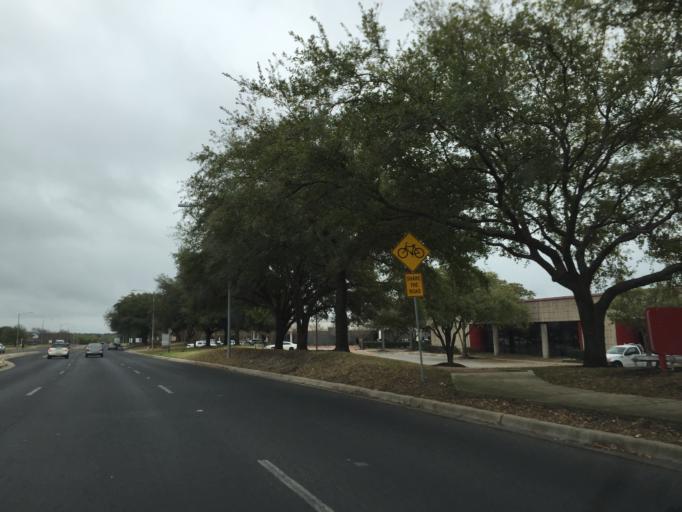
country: US
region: Texas
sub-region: Travis County
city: Wells Branch
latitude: 30.3922
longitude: -97.7081
